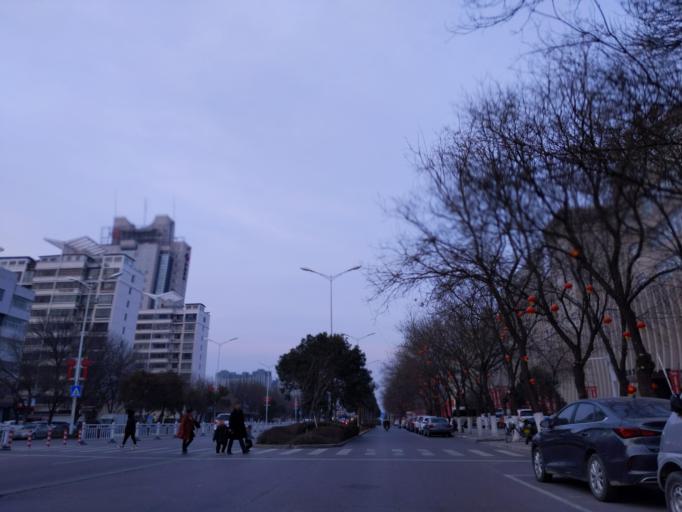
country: CN
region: Henan Sheng
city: Puyang
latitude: 35.7781
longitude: 115.0206
